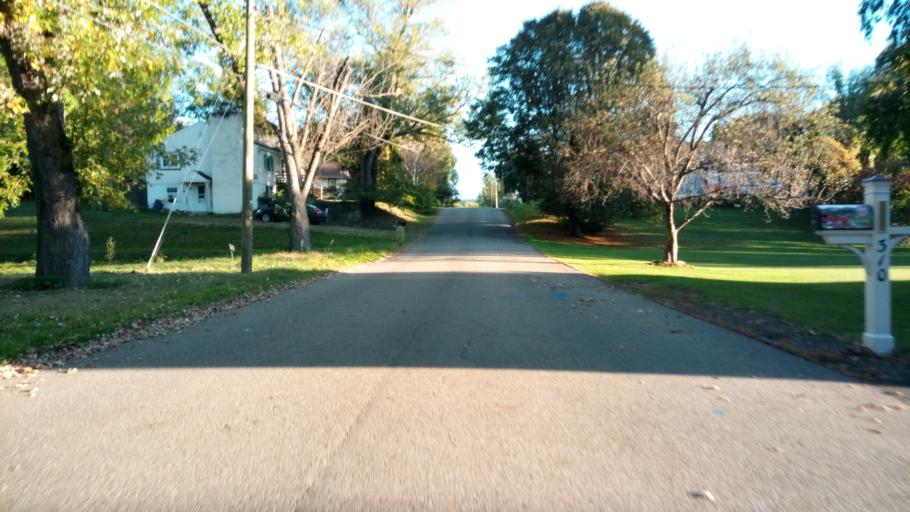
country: US
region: New York
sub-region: Chemung County
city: Elmira
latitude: 42.0776
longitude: -76.8212
